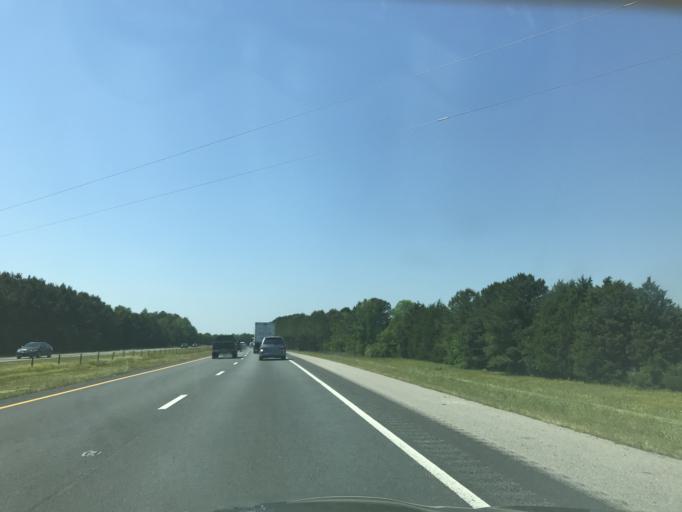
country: US
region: North Carolina
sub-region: Johnston County
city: Benson
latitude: 35.3681
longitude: -78.4945
